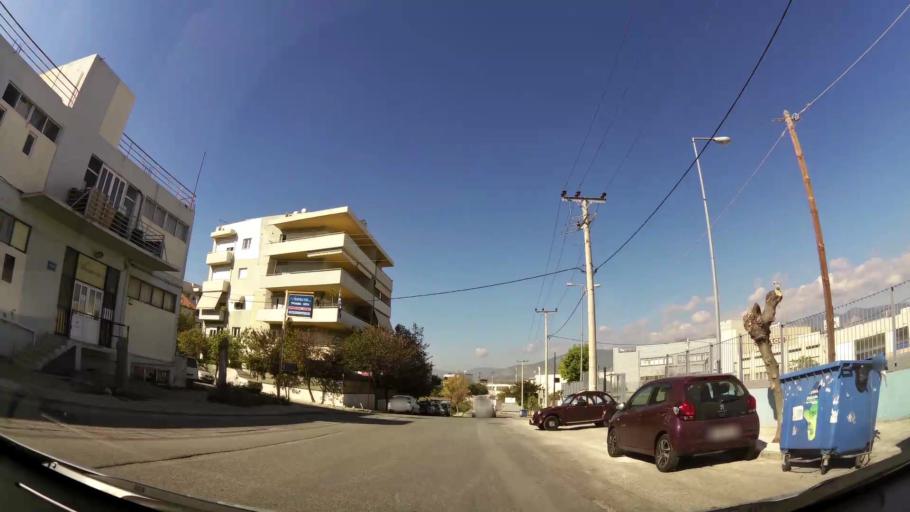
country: GR
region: Attica
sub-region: Nomarchia Athinas
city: Metamorfosi
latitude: 38.0691
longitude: 23.7708
